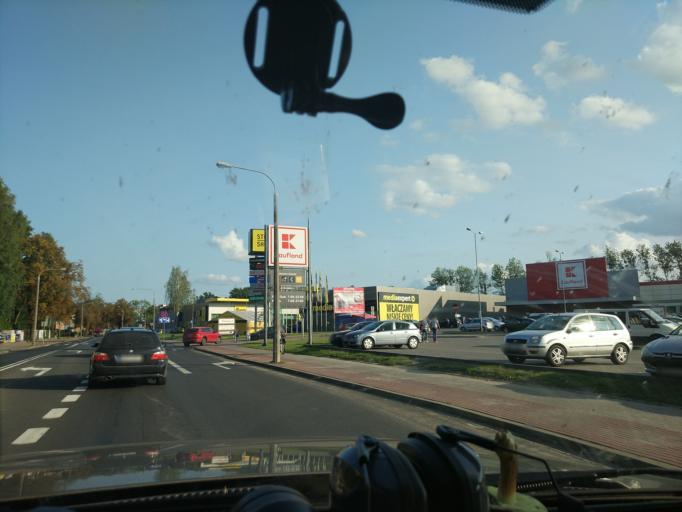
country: PL
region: Warmian-Masurian Voivodeship
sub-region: Powiat szczycienski
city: Szczytno
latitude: 53.5640
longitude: 20.9868
